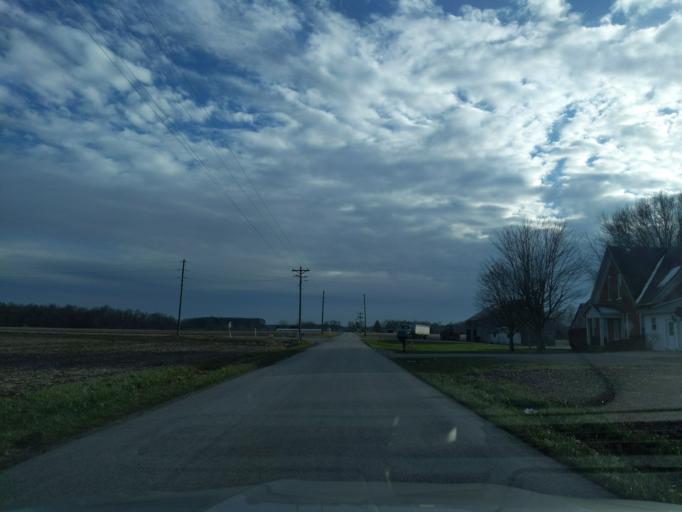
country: US
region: Indiana
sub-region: Decatur County
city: Westport
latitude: 39.2183
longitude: -85.4653
